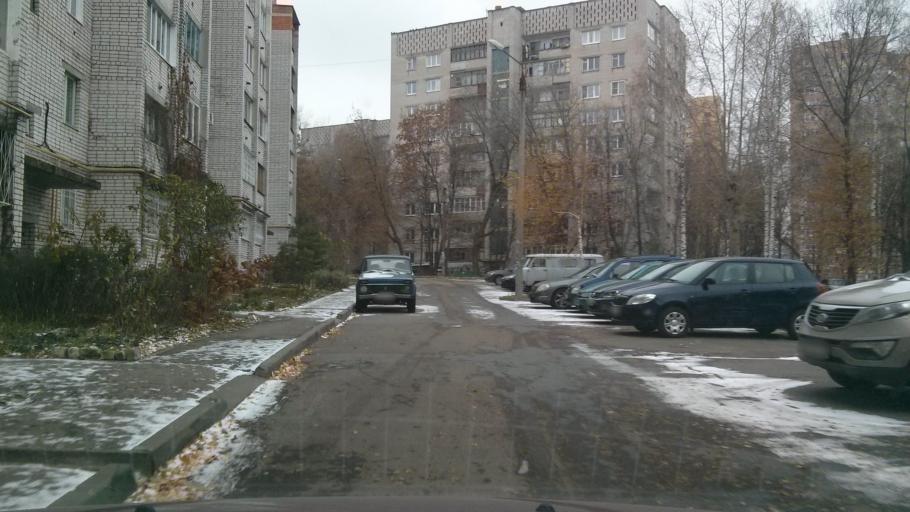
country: RU
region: Nizjnij Novgorod
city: Afonino
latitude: 56.2935
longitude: 44.0487
